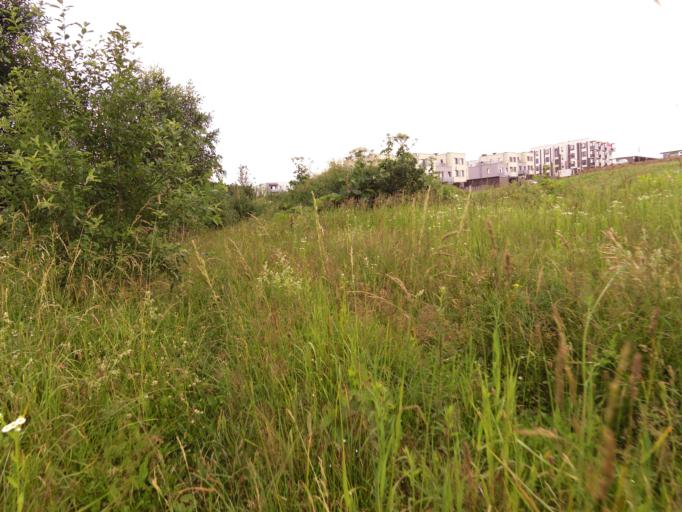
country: LT
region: Vilnius County
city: Pasilaiciai
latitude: 54.7527
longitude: 25.2256
